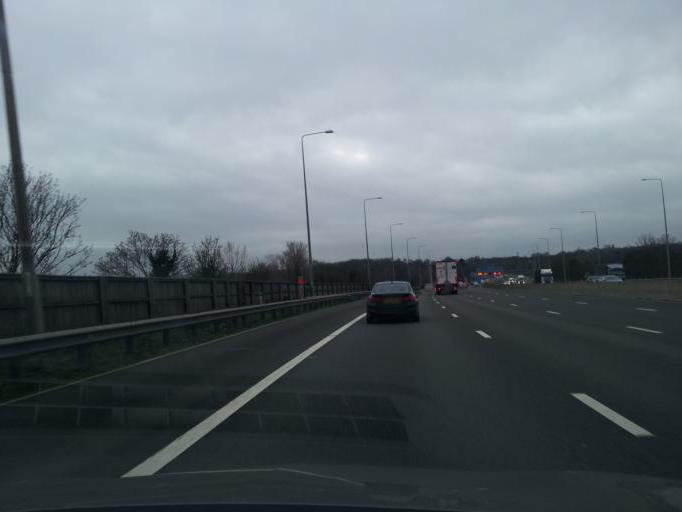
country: GB
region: England
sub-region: Derbyshire
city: Ilkeston
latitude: 52.9397
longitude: -1.2851
